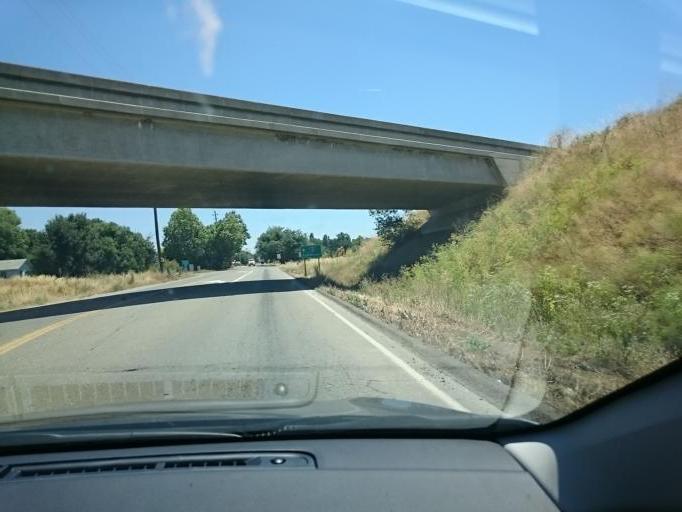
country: US
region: California
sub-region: San Joaquin County
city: Thornton
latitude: 38.2260
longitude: -121.4310
